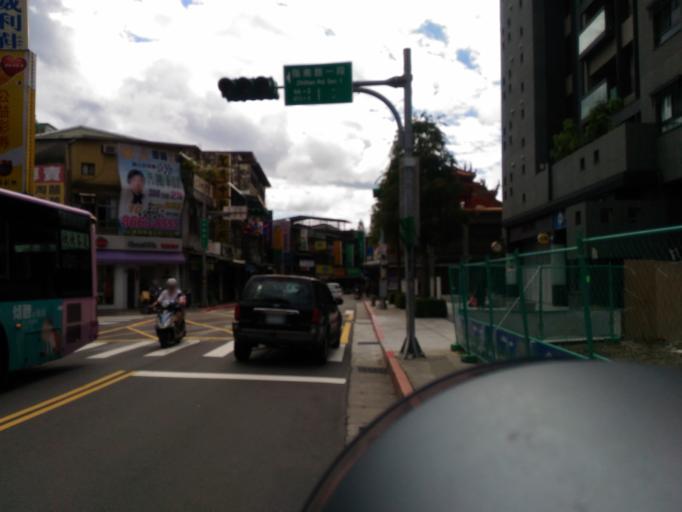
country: TW
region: Taipei
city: Taipei
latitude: 24.9879
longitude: 121.5686
